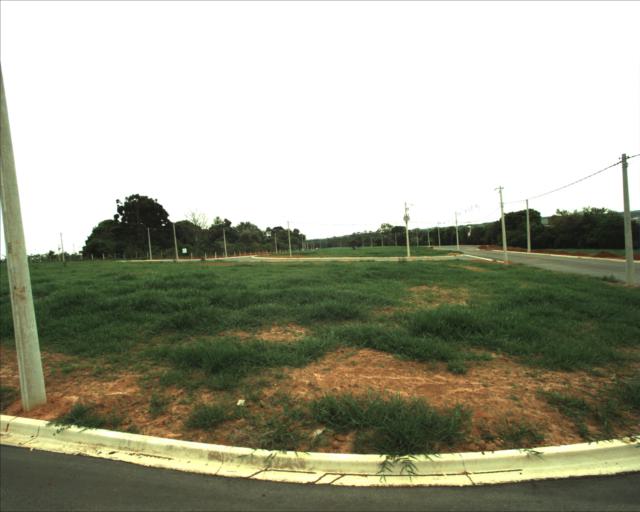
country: BR
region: Sao Paulo
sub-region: Sorocaba
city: Sorocaba
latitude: -23.4208
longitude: -47.4269
